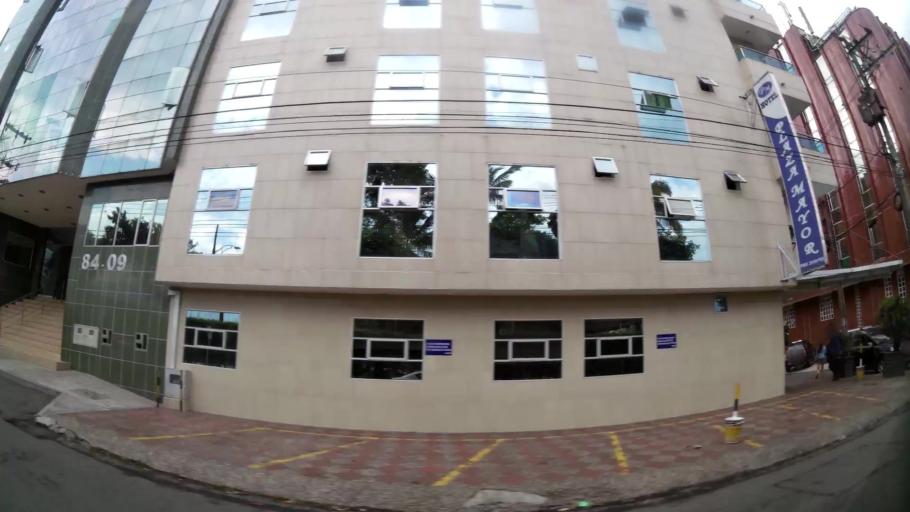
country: CO
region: Antioquia
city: Itagui
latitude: 6.1902
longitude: -75.5913
